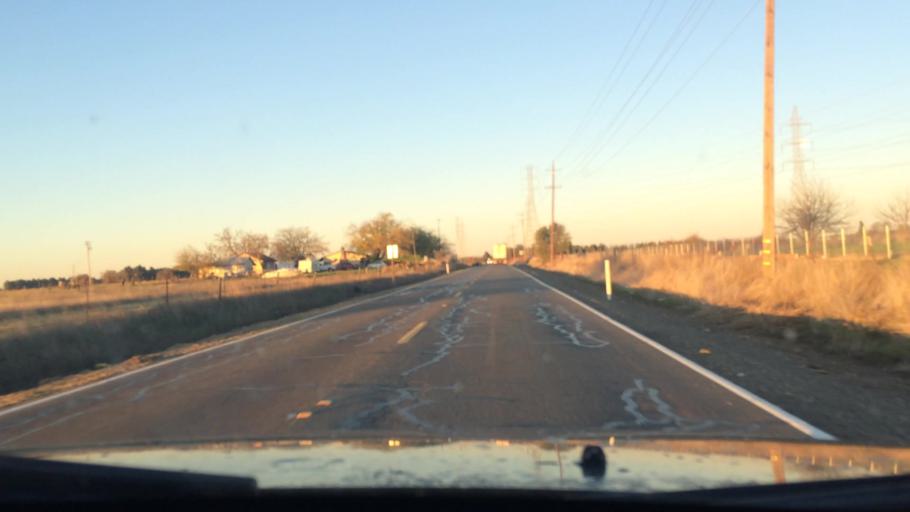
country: US
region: California
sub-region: Sacramento County
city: Vineyard
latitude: 38.5109
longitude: -121.3152
